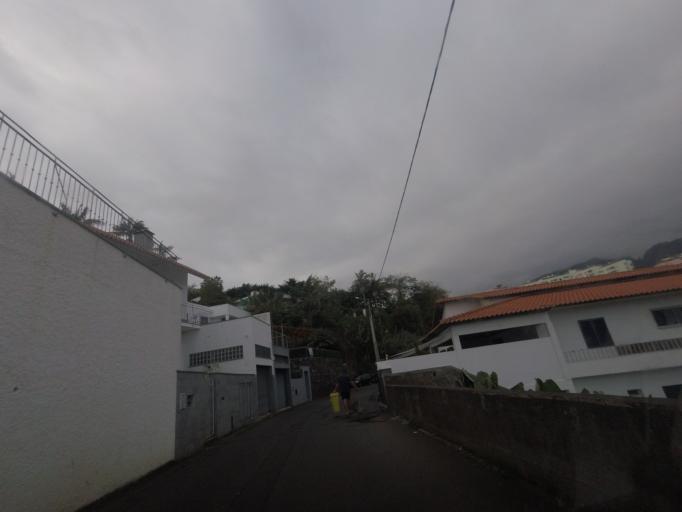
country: PT
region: Madeira
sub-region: Funchal
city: Nossa Senhora do Monte
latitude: 32.6523
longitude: -16.9327
